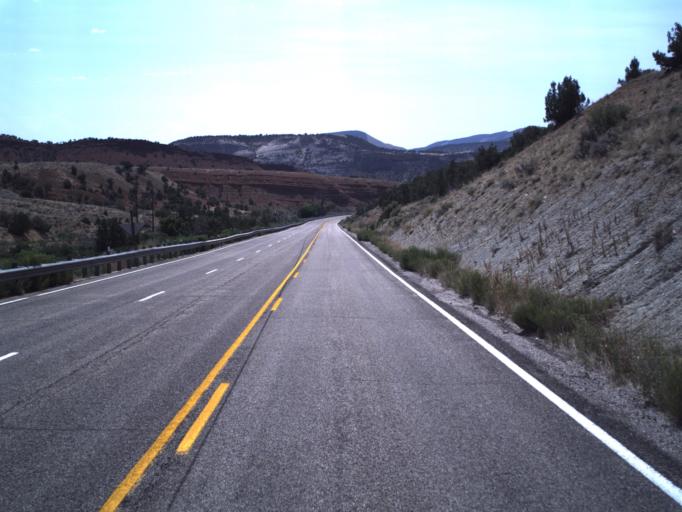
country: US
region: Utah
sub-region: Uintah County
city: Vernal
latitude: 40.6044
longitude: -109.4675
